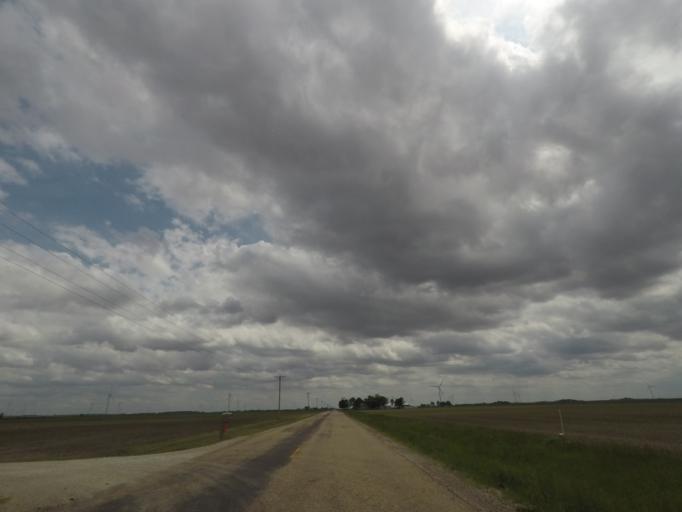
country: US
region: Illinois
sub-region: Macon County
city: Maroa
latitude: 40.0630
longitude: -89.0861
